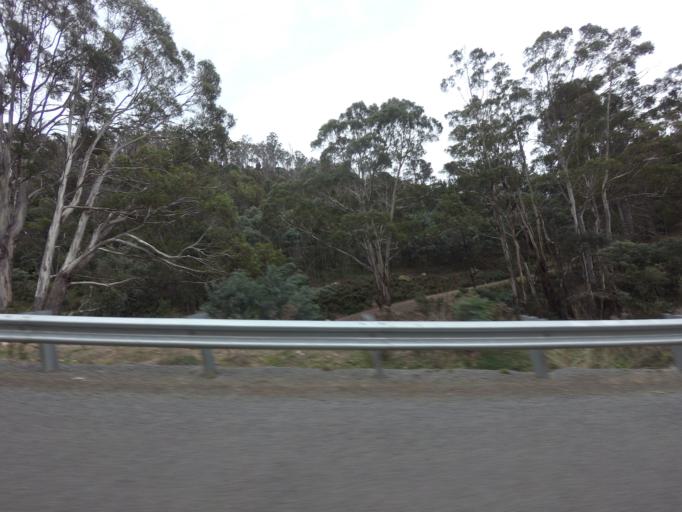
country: AU
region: Tasmania
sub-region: Derwent Valley
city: New Norfolk
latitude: -42.5866
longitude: 147.0163
